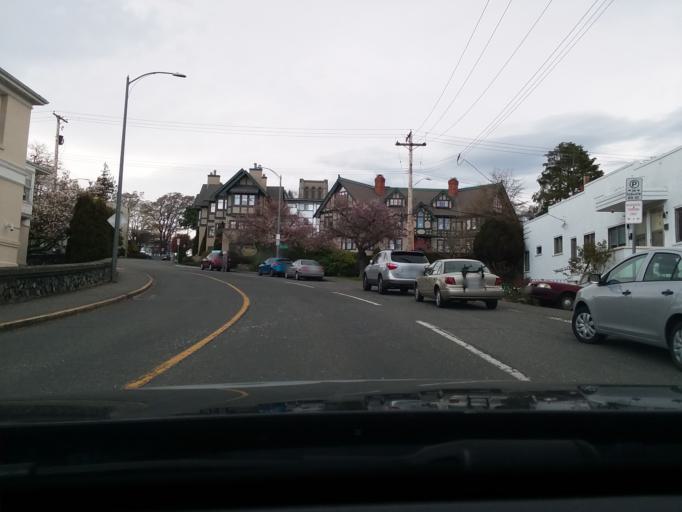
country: CA
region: British Columbia
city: Victoria
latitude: 48.4203
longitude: -123.3602
